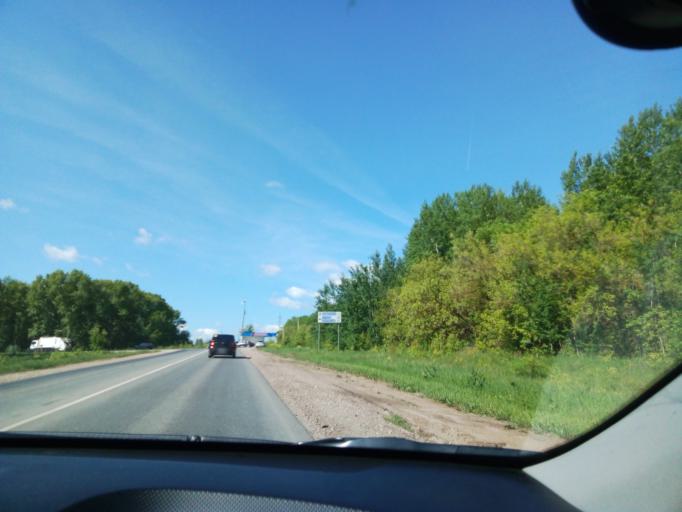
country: RU
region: Chuvashia
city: Novocheboksarsk
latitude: 56.0787
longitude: 47.4978
